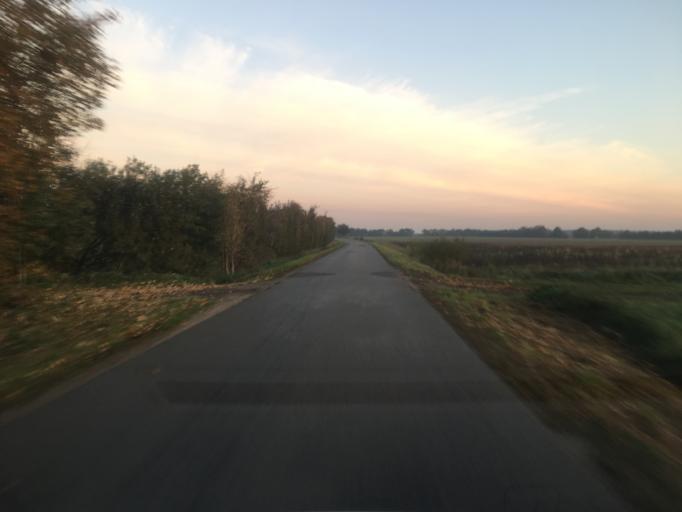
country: DE
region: Schleswig-Holstein
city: Bramstedtlund
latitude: 54.9779
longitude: 9.0675
